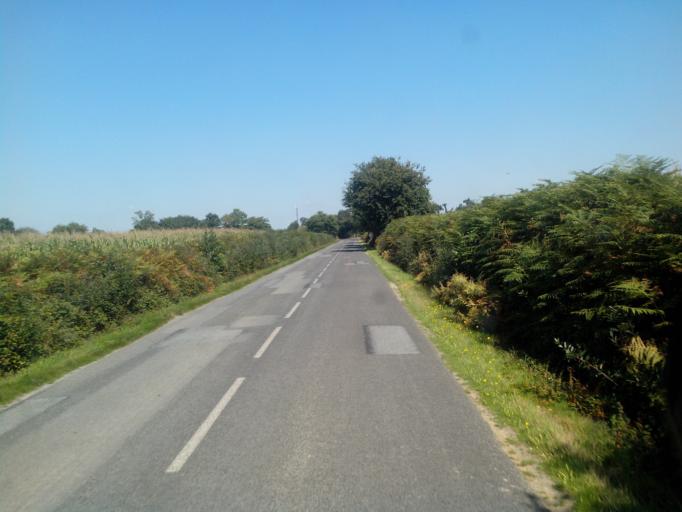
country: FR
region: Brittany
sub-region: Departement d'Ille-et-Vilaine
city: Iffendic
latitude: 48.1043
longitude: -2.0380
